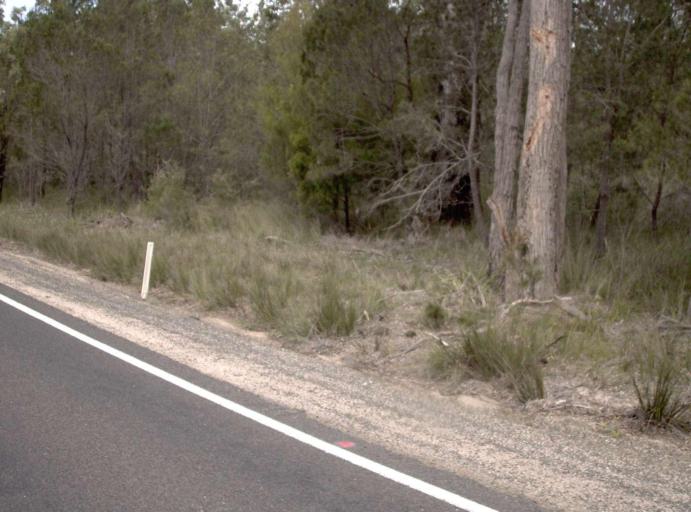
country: AU
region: New South Wales
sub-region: Bega Valley
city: Eden
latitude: -37.4466
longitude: 149.6283
